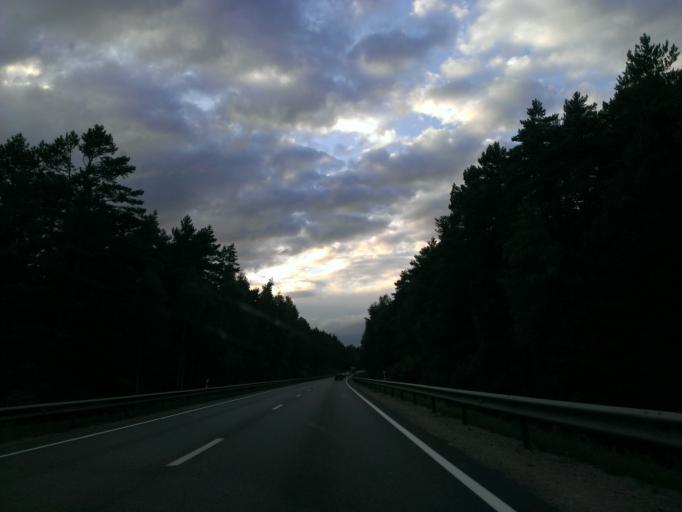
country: LV
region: Riga
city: Bergi
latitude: 56.9808
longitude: 24.3285
